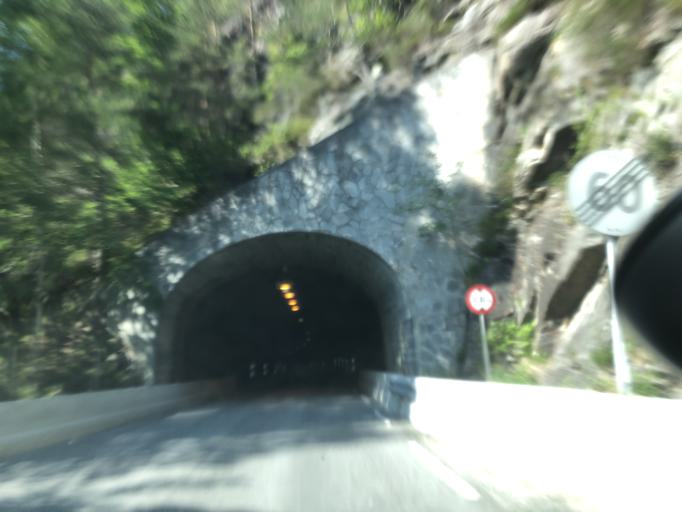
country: NO
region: Hordaland
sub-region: Jondal
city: Jondal
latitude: 60.2879
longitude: 6.2455
